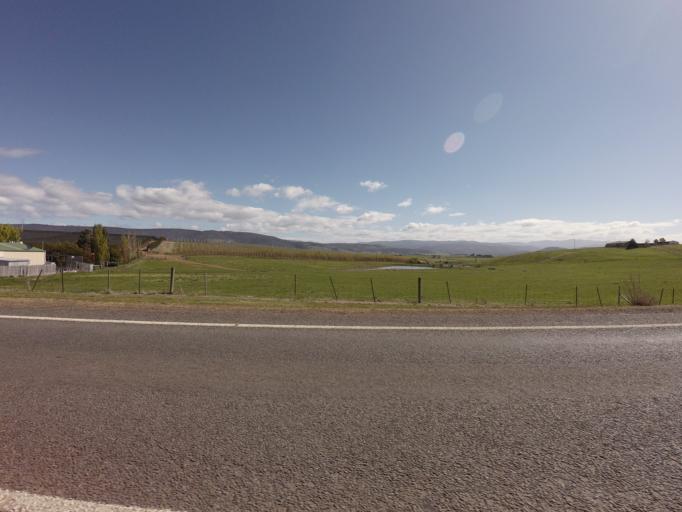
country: AU
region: Tasmania
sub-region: Derwent Valley
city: New Norfolk
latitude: -42.7071
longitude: 146.9447
